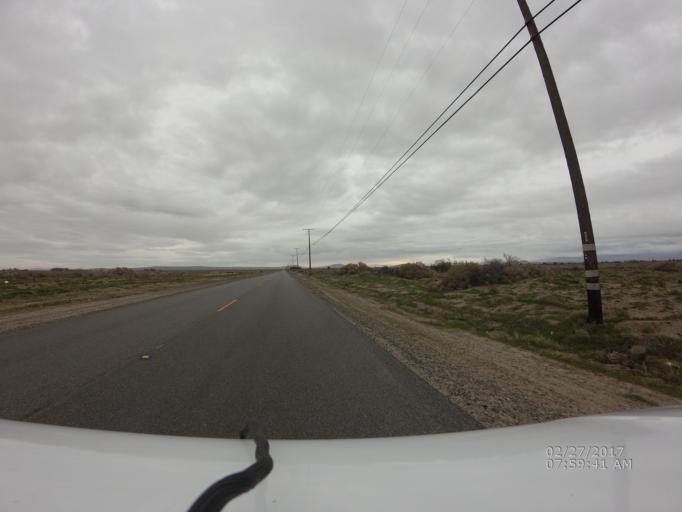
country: US
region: California
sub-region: Los Angeles County
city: Lancaster
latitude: 34.7048
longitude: -117.9861
